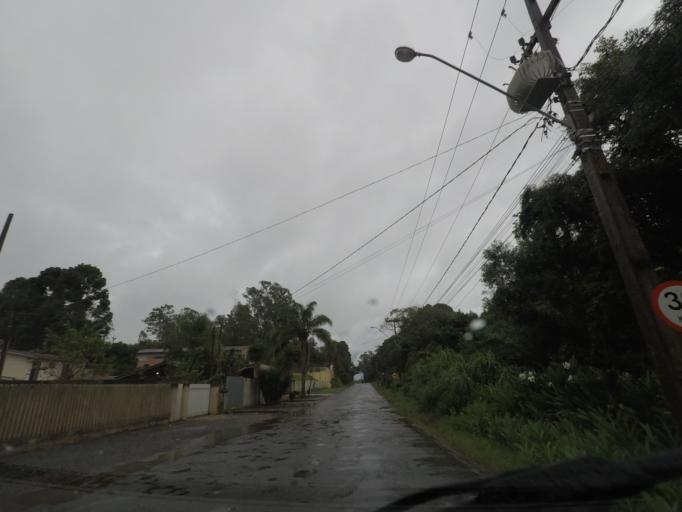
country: BR
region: Parana
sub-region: Campo Largo
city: Campo Largo
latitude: -25.4594
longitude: -49.4270
